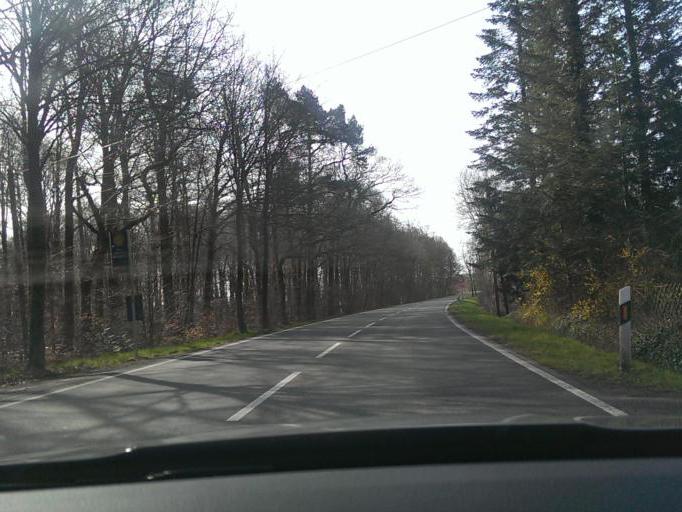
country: DE
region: Lower Saxony
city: Garbsen-Mitte
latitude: 52.5104
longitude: 9.6312
